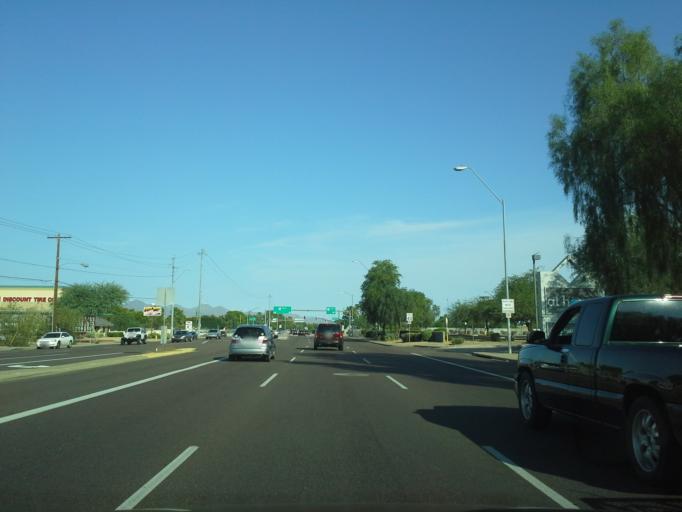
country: US
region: Arizona
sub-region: Maricopa County
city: Paradise Valley
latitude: 33.5969
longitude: -112.0124
